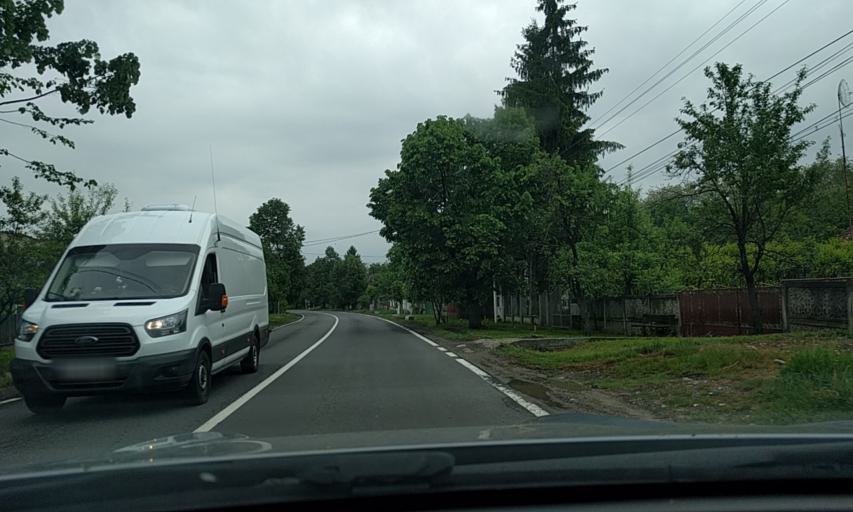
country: RO
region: Dambovita
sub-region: Comuna Branesti
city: Branesti
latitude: 45.0304
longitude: 25.4242
